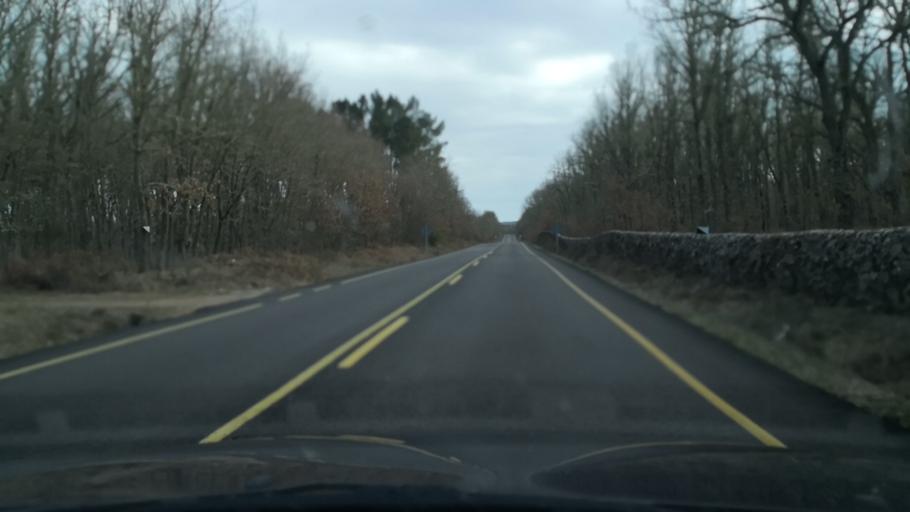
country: ES
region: Castille and Leon
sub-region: Provincia de Salamanca
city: Villasrubias
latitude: 40.3211
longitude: -6.6478
